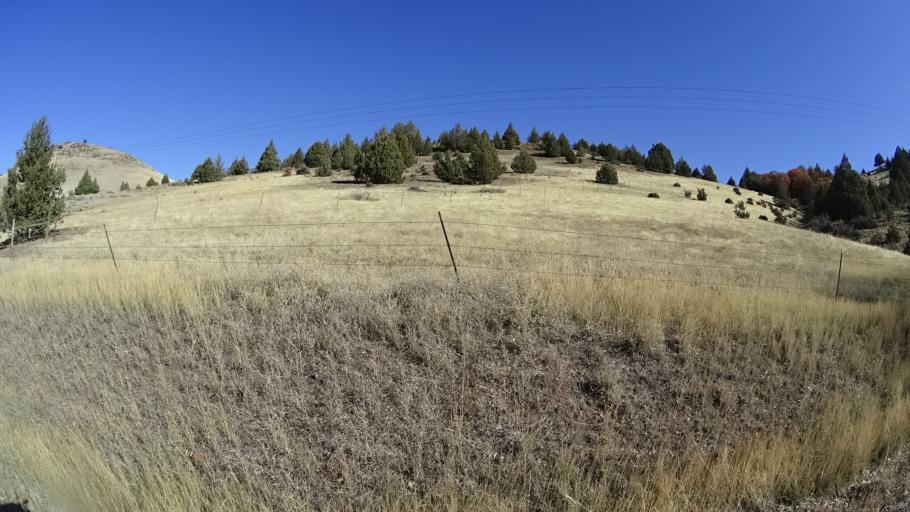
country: US
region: California
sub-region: Siskiyou County
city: Montague
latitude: 41.7897
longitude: -122.3599
